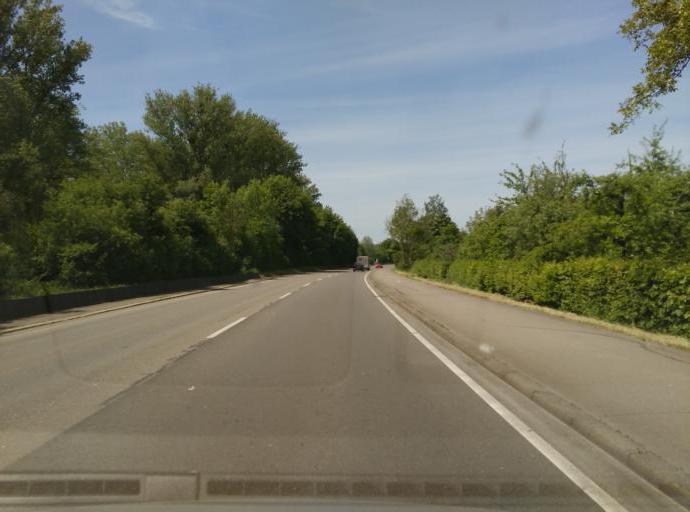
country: DE
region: Baden-Wuerttemberg
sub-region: Regierungsbezirk Stuttgart
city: Grossbettlingen
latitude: 48.6168
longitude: 9.3081
